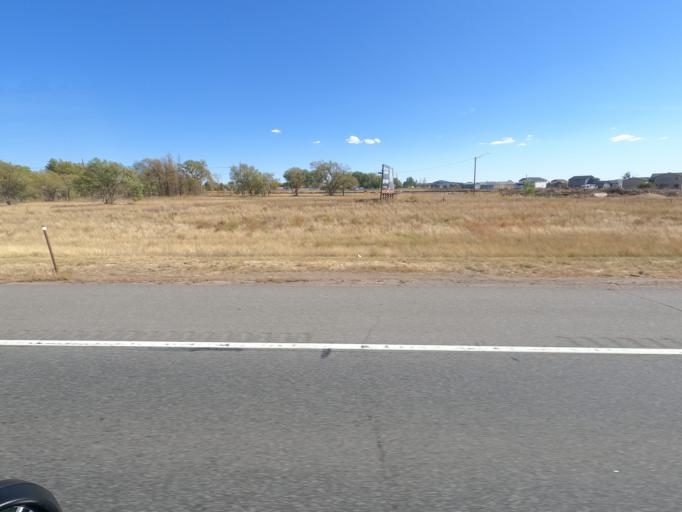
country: US
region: Colorado
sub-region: Weld County
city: Hudson
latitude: 40.0676
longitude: -104.6505
